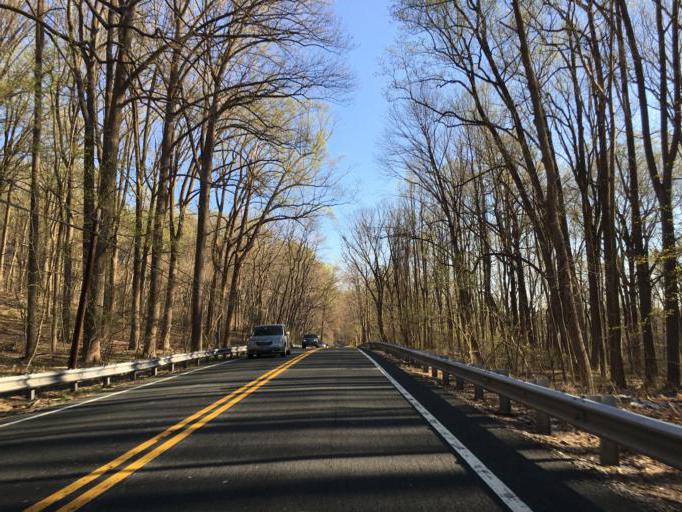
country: US
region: Maryland
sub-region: Baltimore County
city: Timonium
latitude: 39.4575
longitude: -76.5912
